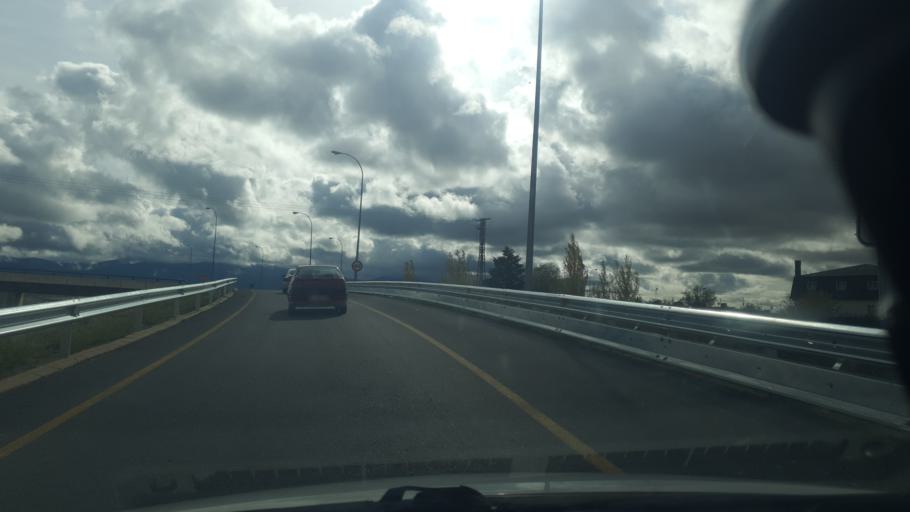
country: ES
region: Castille and Leon
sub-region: Provincia de Segovia
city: San Cristobal de Segovia
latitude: 40.9538
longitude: -4.0910
